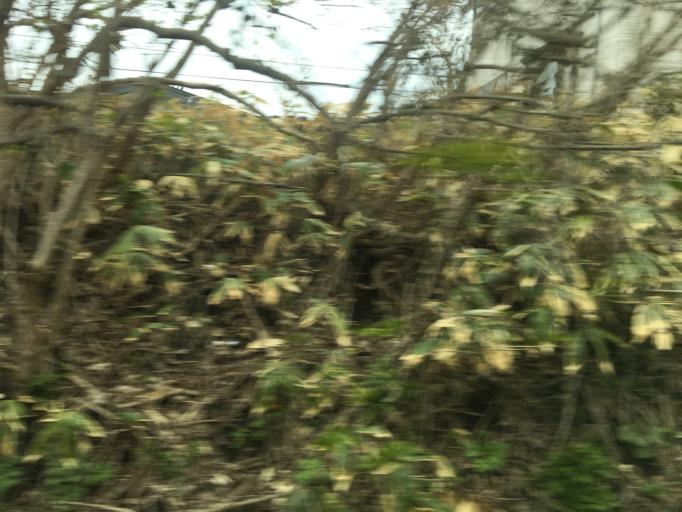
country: JP
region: Akita
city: Noshiromachi
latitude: 40.6290
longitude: 139.8885
